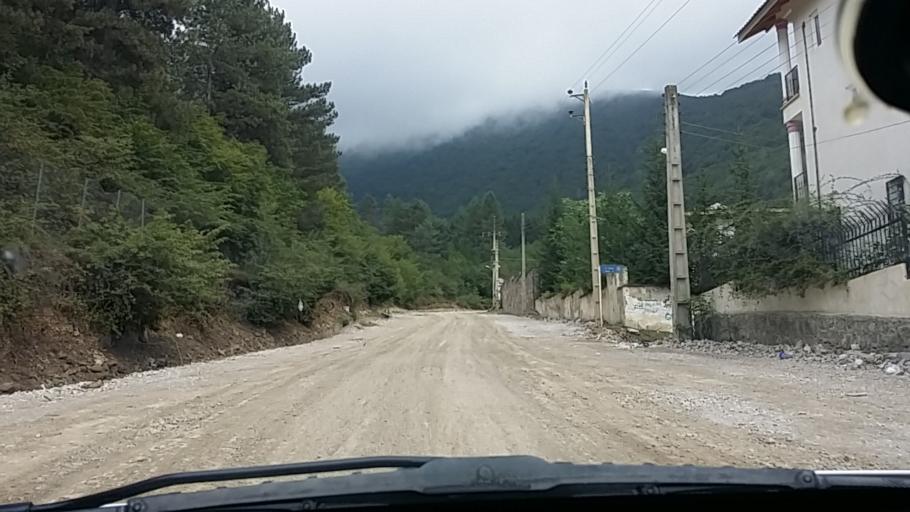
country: IR
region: Mazandaran
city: `Abbasabad
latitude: 36.4919
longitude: 51.1669
